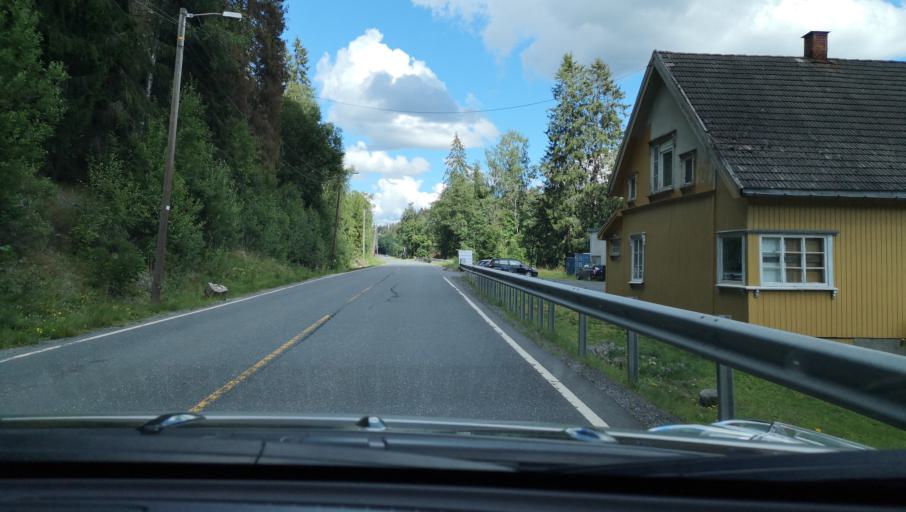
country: NO
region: Ostfold
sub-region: Hobol
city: Tomter
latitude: 59.6504
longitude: 10.9931
